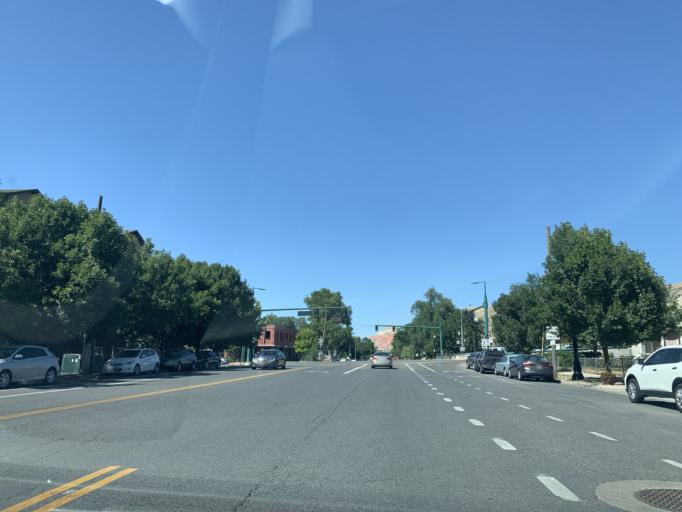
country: US
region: Utah
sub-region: Salt Lake County
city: Salt Lake City
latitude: 40.7708
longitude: -111.9082
